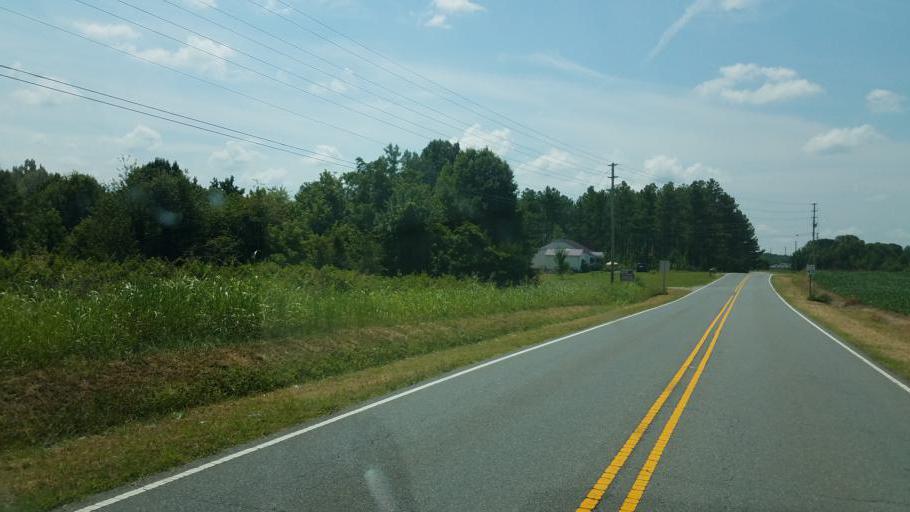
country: US
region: North Carolina
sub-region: Cleveland County
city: Kings Mountain
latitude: 35.2849
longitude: -81.3562
